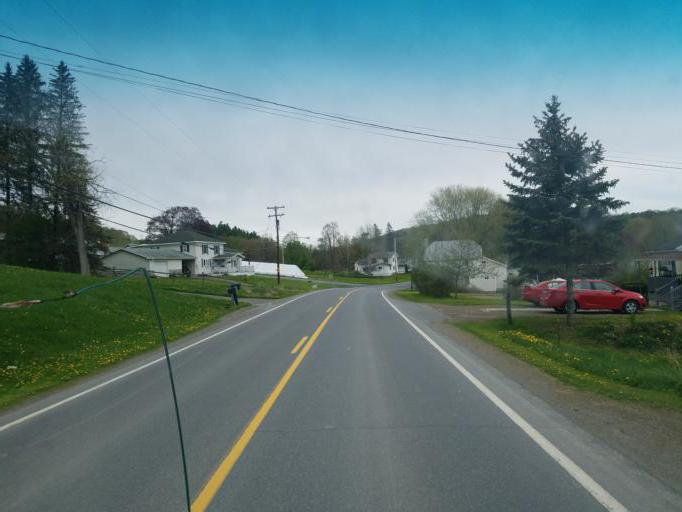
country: US
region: Pennsylvania
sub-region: Tioga County
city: Westfield
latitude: 41.8666
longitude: -77.5323
